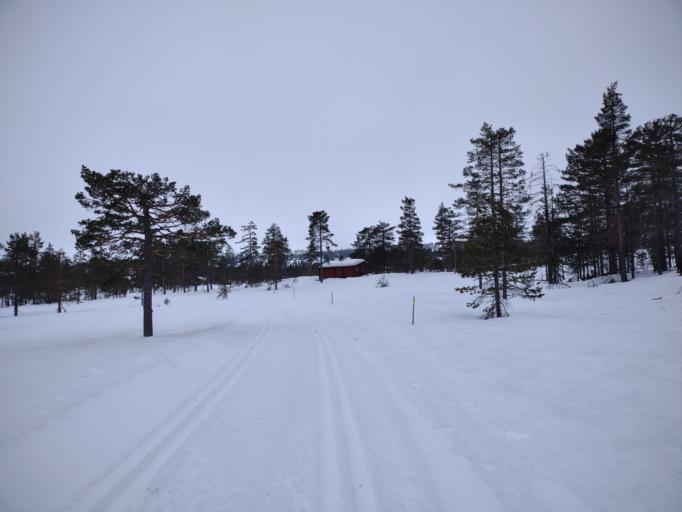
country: NO
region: Buskerud
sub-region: Flesberg
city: Lampeland
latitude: 59.7959
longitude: 9.4341
